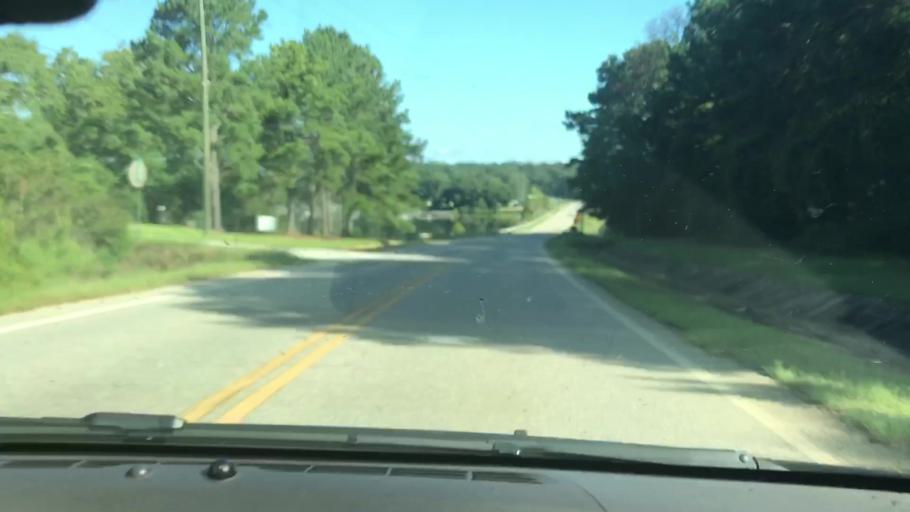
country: US
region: Georgia
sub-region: Clay County
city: Fort Gaines
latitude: 31.7415
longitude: -85.0501
